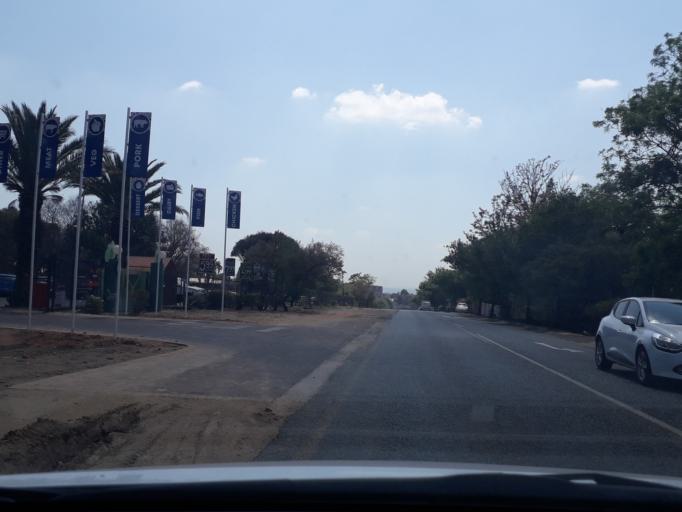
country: ZA
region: Gauteng
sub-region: West Rand District Municipality
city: Muldersdriseloop
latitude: -26.0744
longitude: 27.9320
